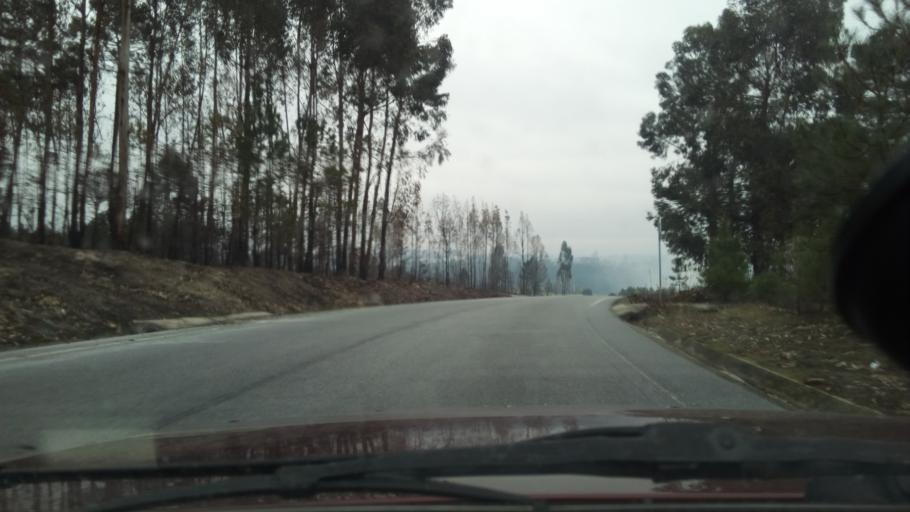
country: PT
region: Viseu
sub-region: Mangualde
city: Mangualde
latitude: 40.6012
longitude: -7.8081
